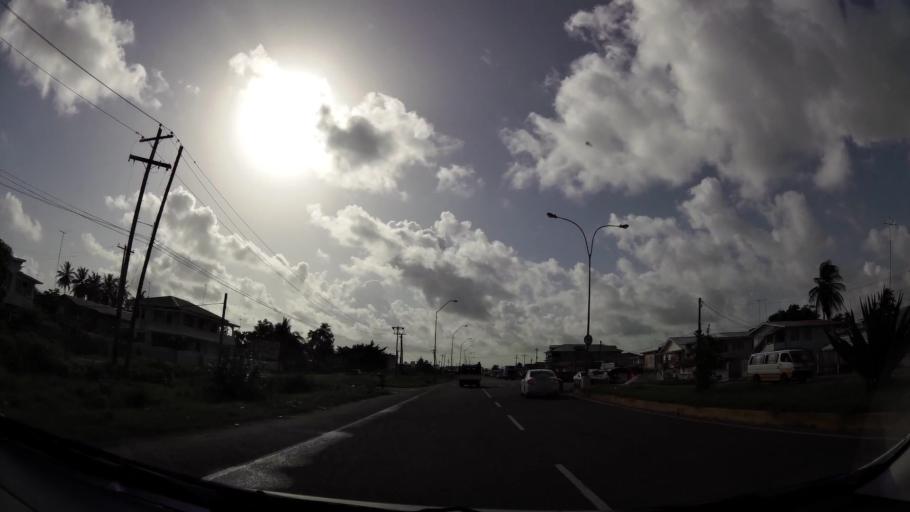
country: GY
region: Demerara-Mahaica
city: Georgetown
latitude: 6.8190
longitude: -58.0898
